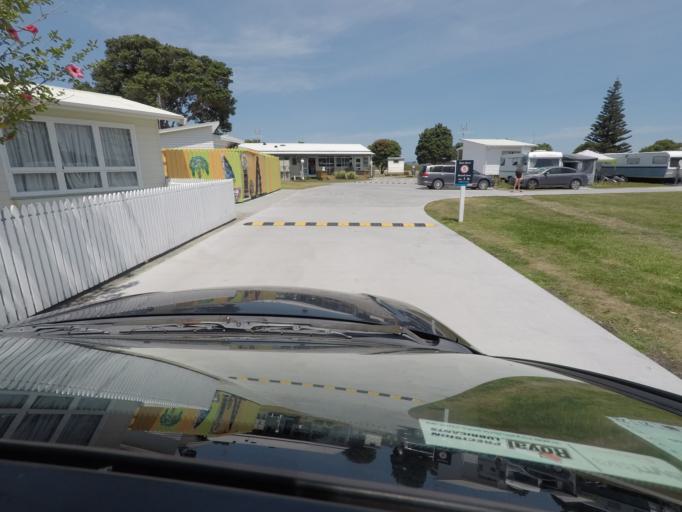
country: NZ
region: Auckland
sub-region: Auckland
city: Warkworth
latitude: -36.3150
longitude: 174.7653
